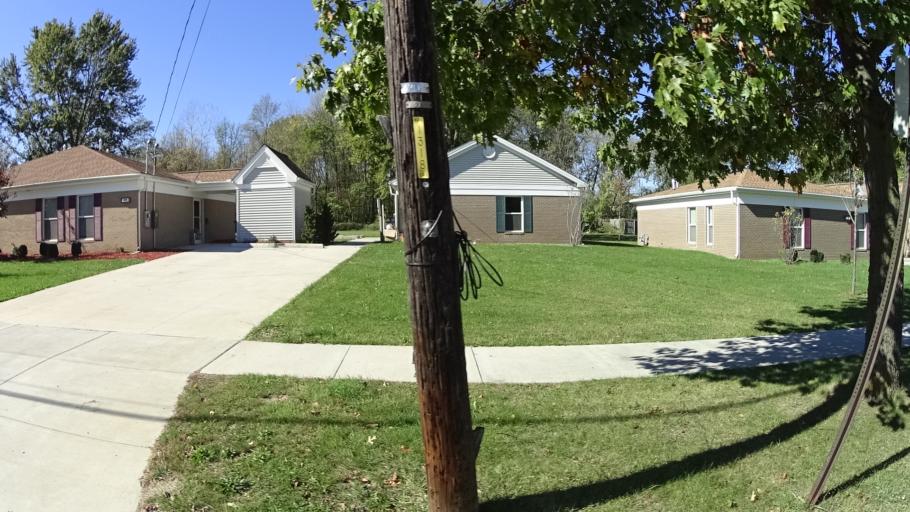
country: US
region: Ohio
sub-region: Lorain County
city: Oberlin
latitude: 41.2856
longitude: -82.2127
